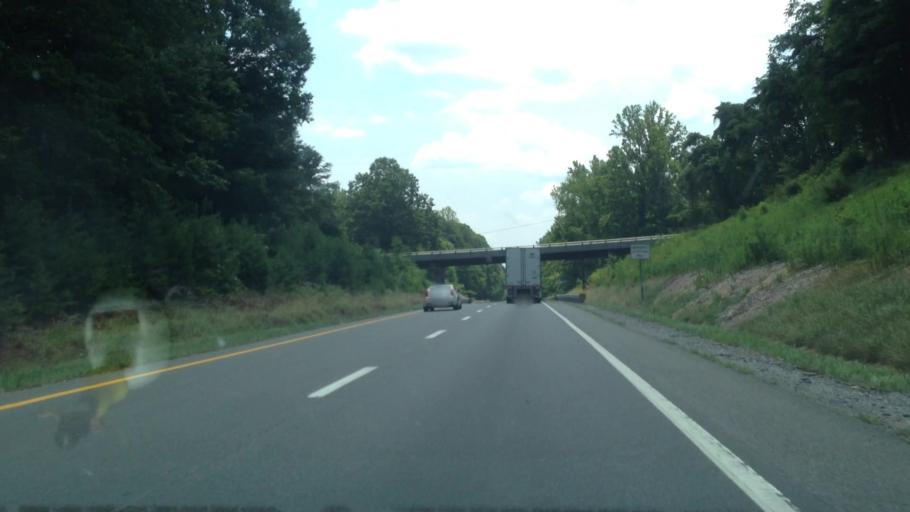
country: US
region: Virginia
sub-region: Henry County
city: Horse Pasture
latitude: 36.6438
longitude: -79.9016
